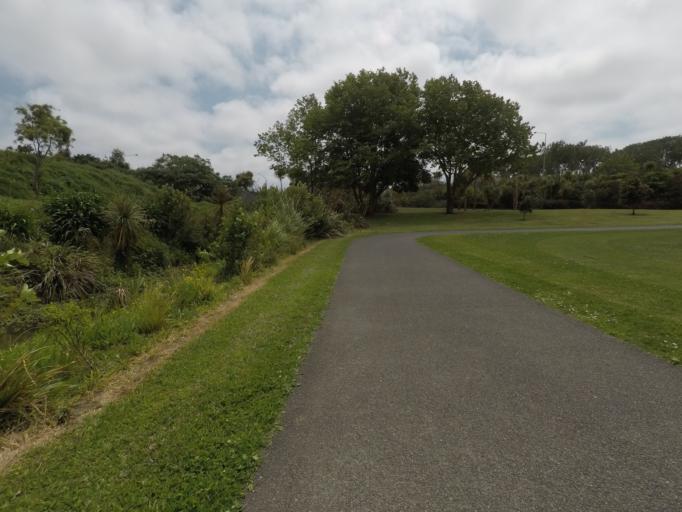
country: NZ
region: Auckland
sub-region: Auckland
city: Auckland
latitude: -36.9138
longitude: 174.7428
